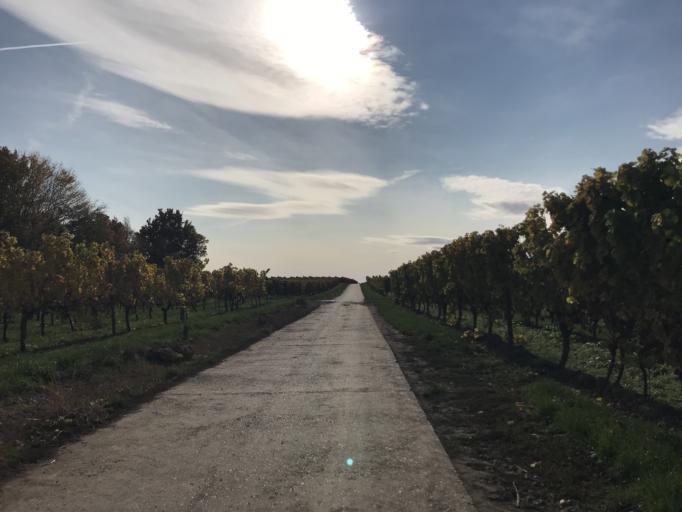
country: DE
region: Rheinland-Pfalz
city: Essenheim
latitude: 49.9249
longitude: 8.1494
